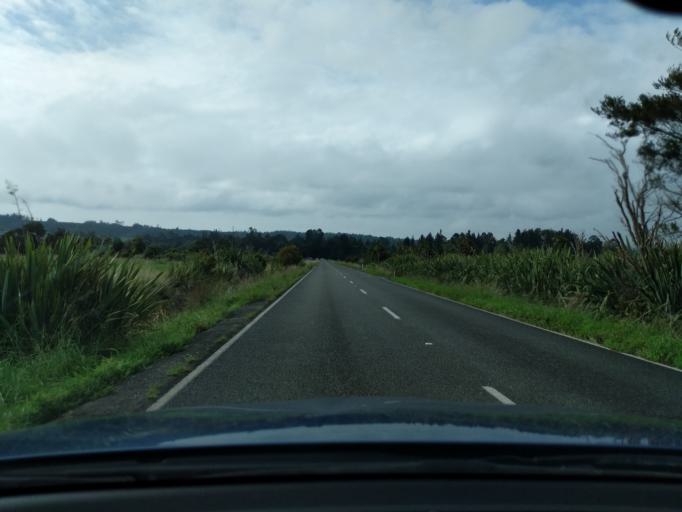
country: NZ
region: Tasman
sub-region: Tasman District
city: Takaka
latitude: -40.6776
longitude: 172.6628
